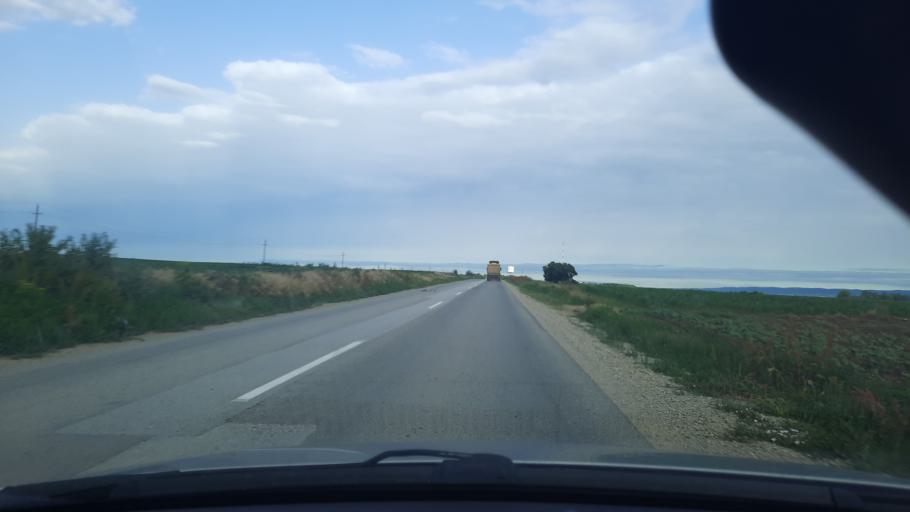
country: RS
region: Autonomna Pokrajina Vojvodina
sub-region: Sremski Okrug
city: Ruma
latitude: 45.0090
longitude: 19.8919
